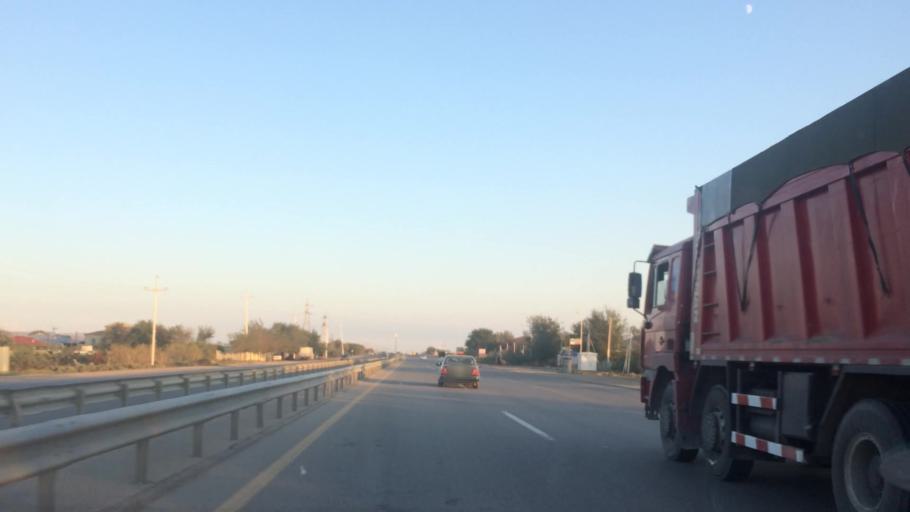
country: AZ
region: Haciqabul
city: Haciqabul
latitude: 40.0148
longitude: 49.1389
